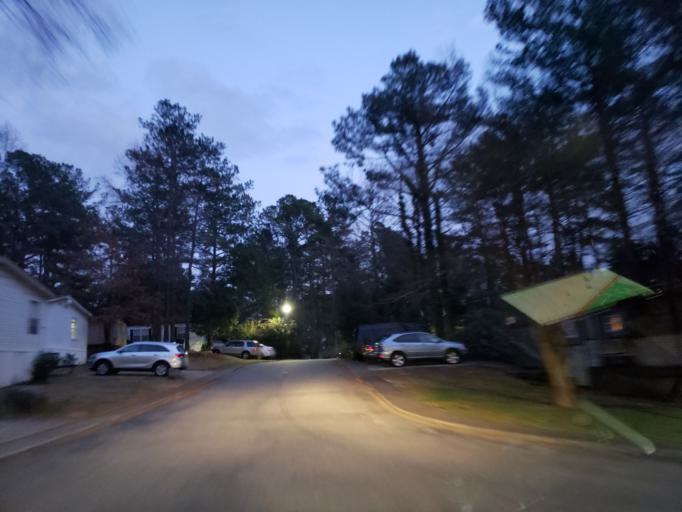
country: US
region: Georgia
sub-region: Cobb County
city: Kennesaw
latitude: 34.0235
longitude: -84.6323
